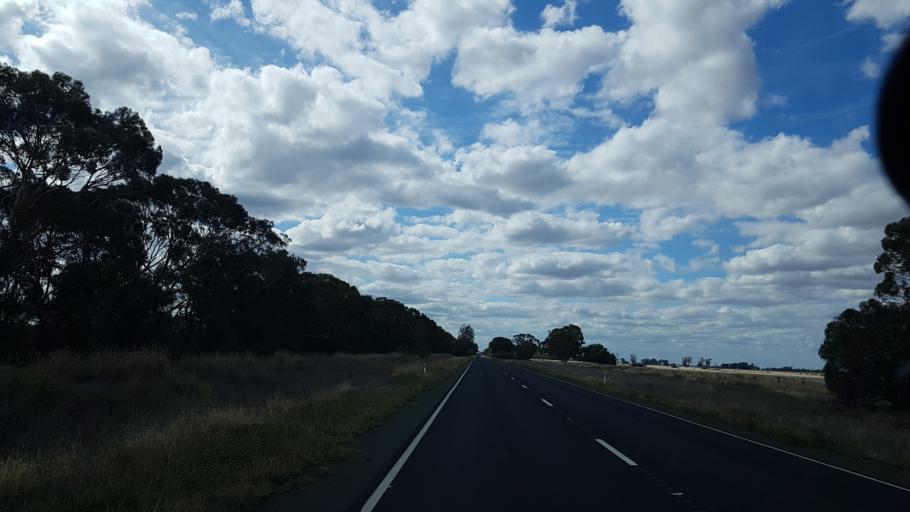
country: AU
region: Victoria
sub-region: Swan Hill
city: Swan Hill
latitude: -35.9846
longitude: 143.9454
